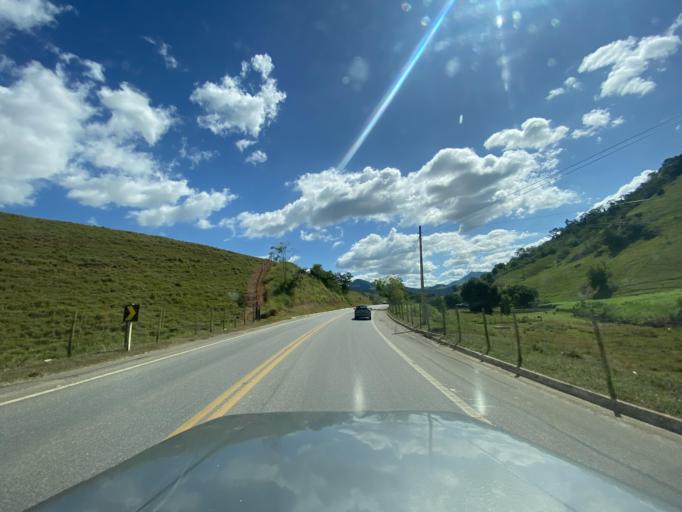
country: BR
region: Espirito Santo
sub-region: Jeronimo Monteiro
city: Jeronimo Monteiro
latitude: -20.7744
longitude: -41.4244
